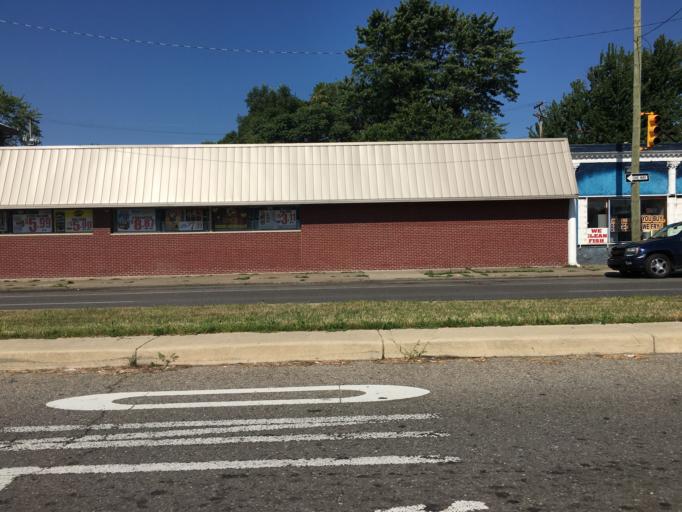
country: US
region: Michigan
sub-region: Wayne County
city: Highland Park
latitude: 42.4116
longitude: -83.1405
